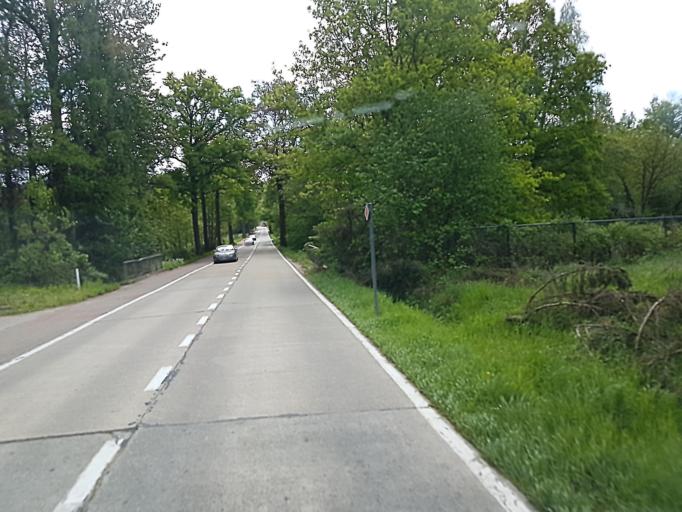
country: BE
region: Flanders
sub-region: Provincie Vlaams-Brabant
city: Diest
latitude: 51.0078
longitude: 5.0256
